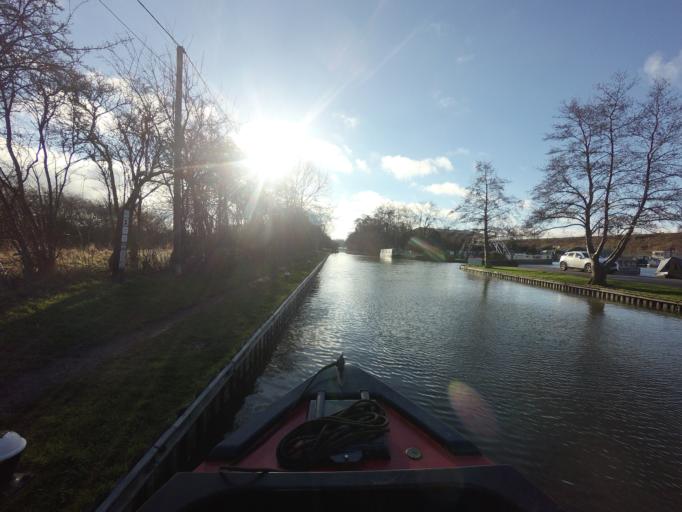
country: GB
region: England
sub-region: Northamptonshire
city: Long Buckby
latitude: 52.2726
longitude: -1.0950
